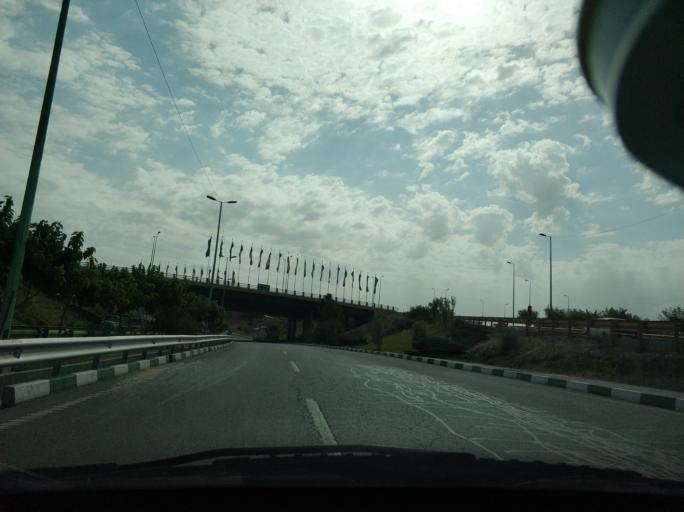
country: IR
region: Tehran
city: Tehran
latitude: 35.7237
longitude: 51.5851
